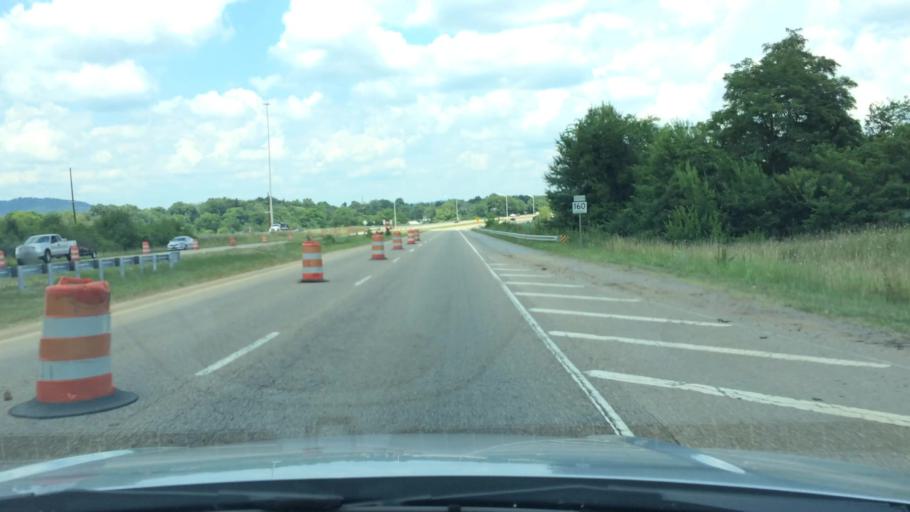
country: US
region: Tennessee
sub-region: Hamblen County
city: Morristown
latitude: 36.1755
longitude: -83.3462
